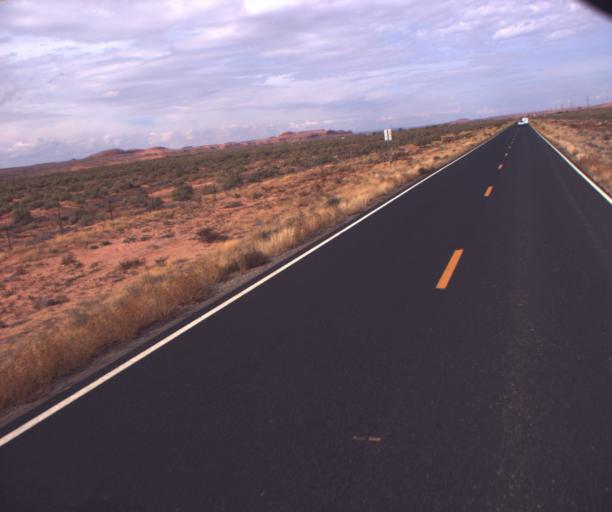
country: US
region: Arizona
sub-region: Apache County
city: Many Farms
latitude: 36.6629
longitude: -109.5964
